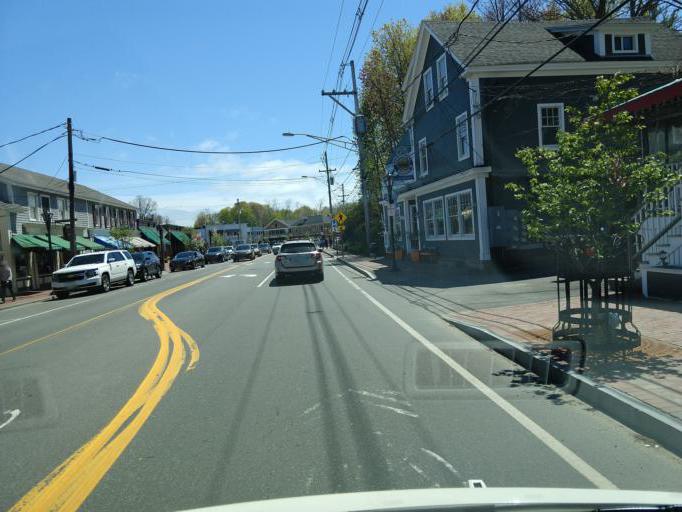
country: US
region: Maine
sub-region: York County
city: Ogunquit
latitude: 43.2499
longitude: -70.6000
